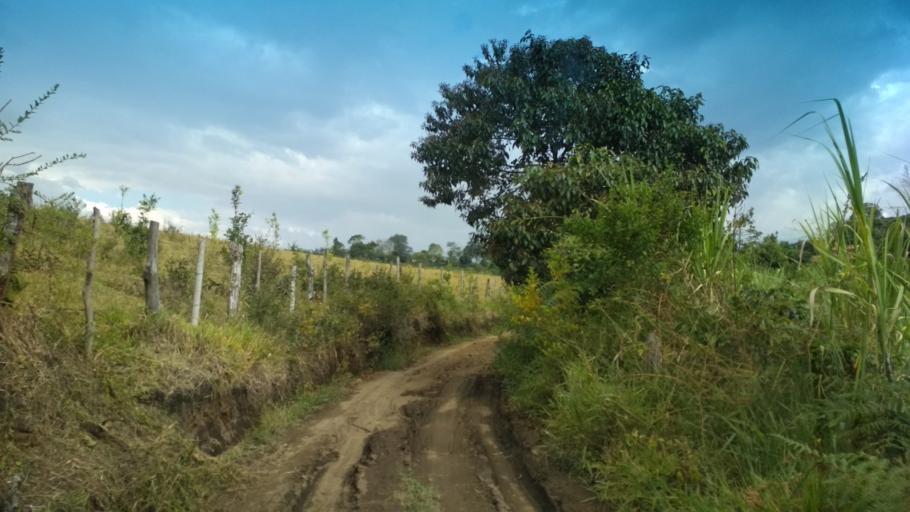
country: CO
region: Cauca
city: Lopez
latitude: 2.4056
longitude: -76.7141
